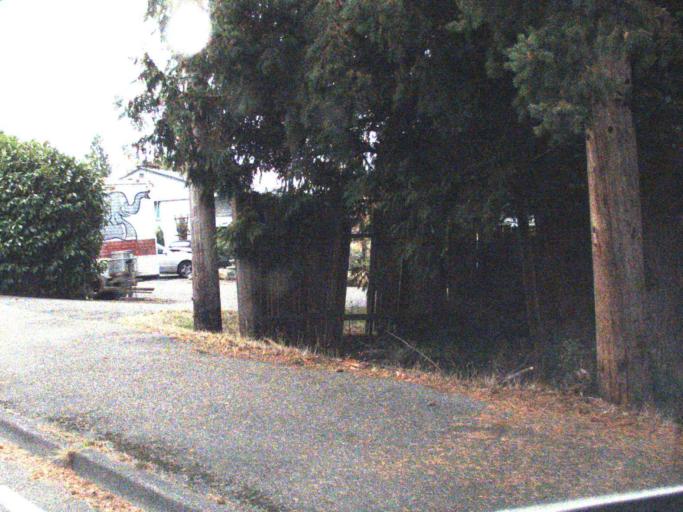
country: US
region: Washington
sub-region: Snohomish County
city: Mukilteo
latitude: 47.9453
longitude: -122.3042
